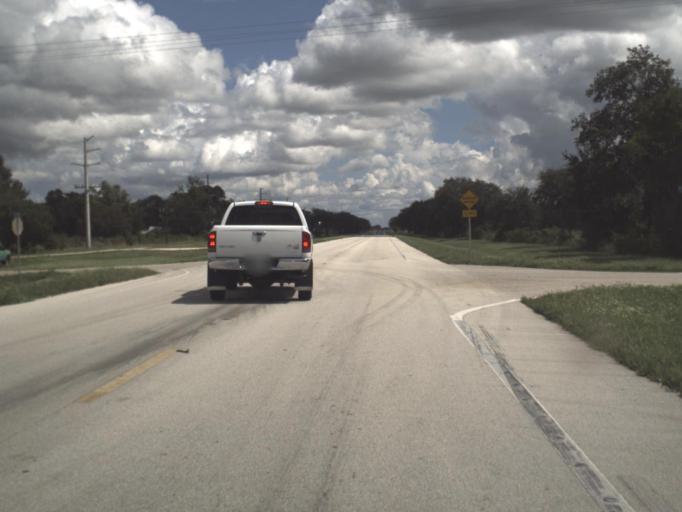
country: US
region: Florida
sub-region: DeSoto County
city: Southeast Arcadia
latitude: 27.2087
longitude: -81.7678
